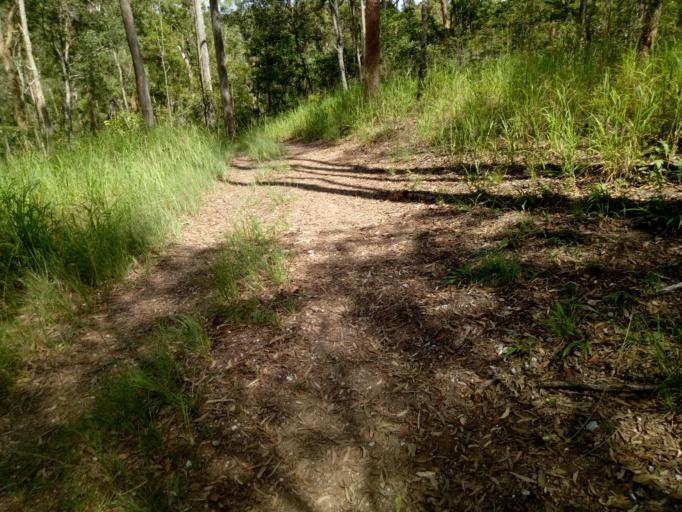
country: AU
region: Queensland
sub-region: Moreton Bay
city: Ferny Hills
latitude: -27.4454
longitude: 152.9100
